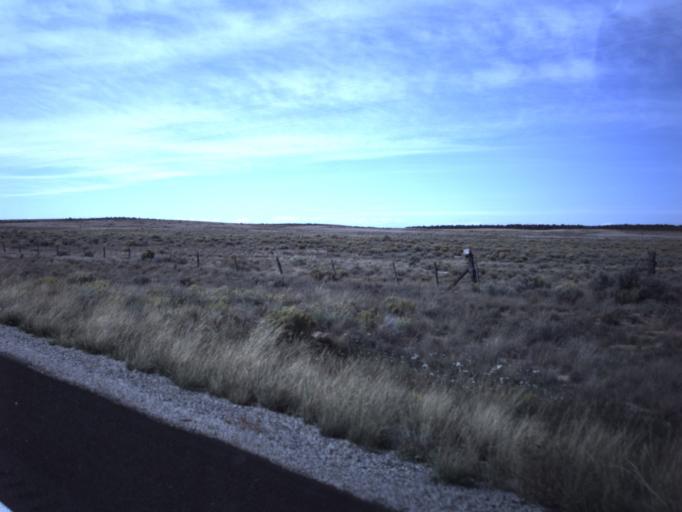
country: US
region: Utah
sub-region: San Juan County
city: Monticello
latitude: 37.8505
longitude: -109.1664
